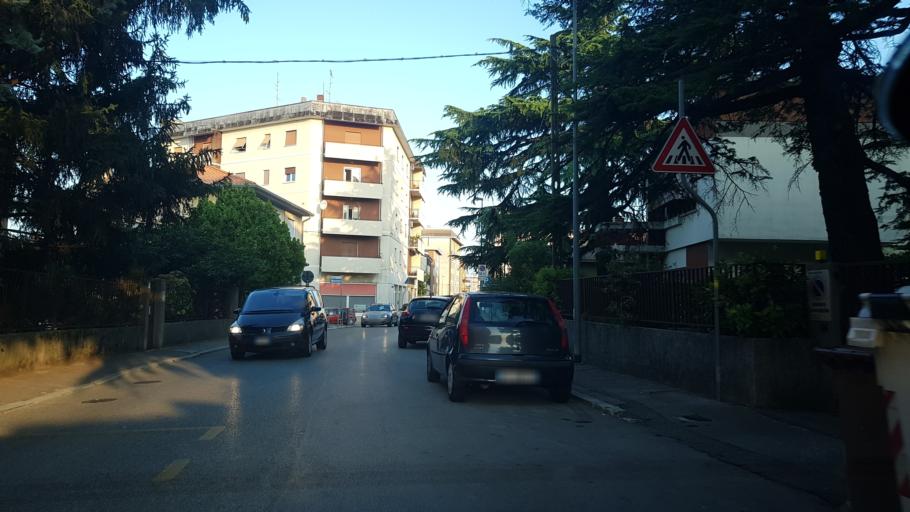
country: IT
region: Friuli Venezia Giulia
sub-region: Provincia di Gorizia
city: Monfalcone
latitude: 45.8063
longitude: 13.5419
